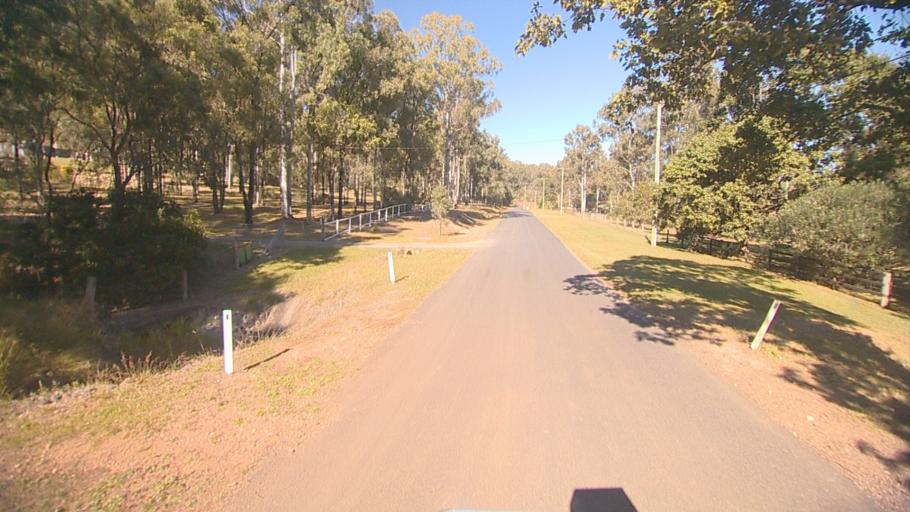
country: AU
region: Queensland
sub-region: Logan
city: Windaroo
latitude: -27.7823
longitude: 153.1479
